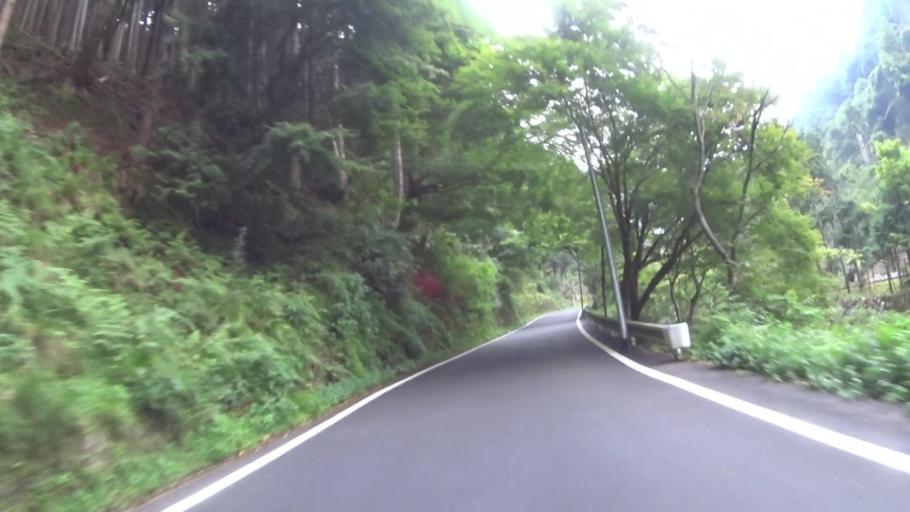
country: JP
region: Kyoto
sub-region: Kyoto-shi
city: Kamigyo-ku
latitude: 35.1061
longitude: 135.7630
